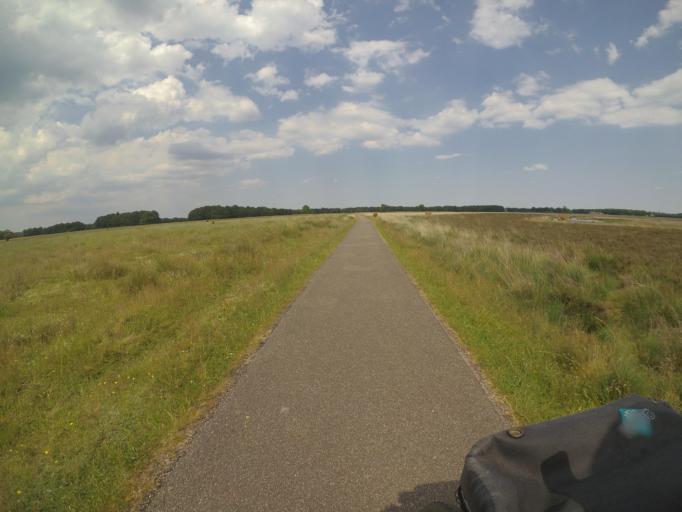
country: NL
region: Drenthe
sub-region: Gemeente Assen
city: Assen
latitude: 52.9218
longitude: 6.5002
